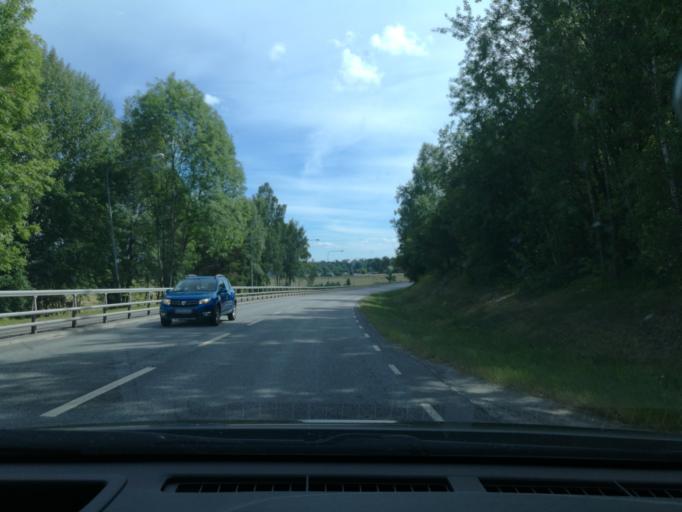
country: SE
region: Stockholm
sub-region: Upplands Vasby Kommun
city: Upplands Vaesby
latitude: 59.5352
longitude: 17.9227
